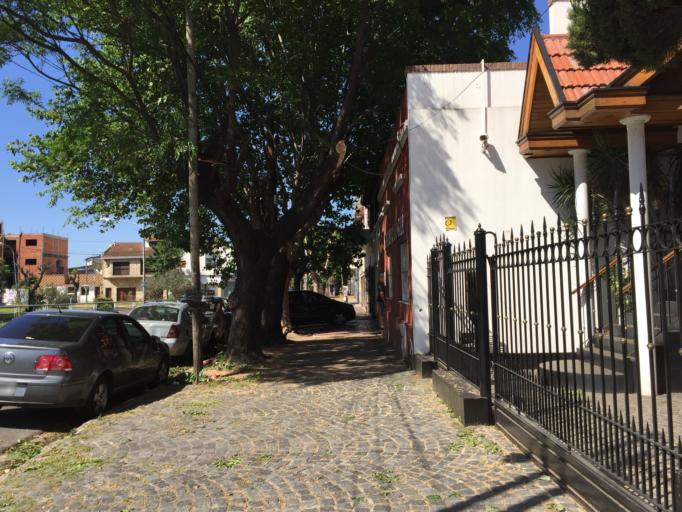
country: AR
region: Buenos Aires
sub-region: Partido de Lanus
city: Lanus
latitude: -34.7042
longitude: -58.3891
